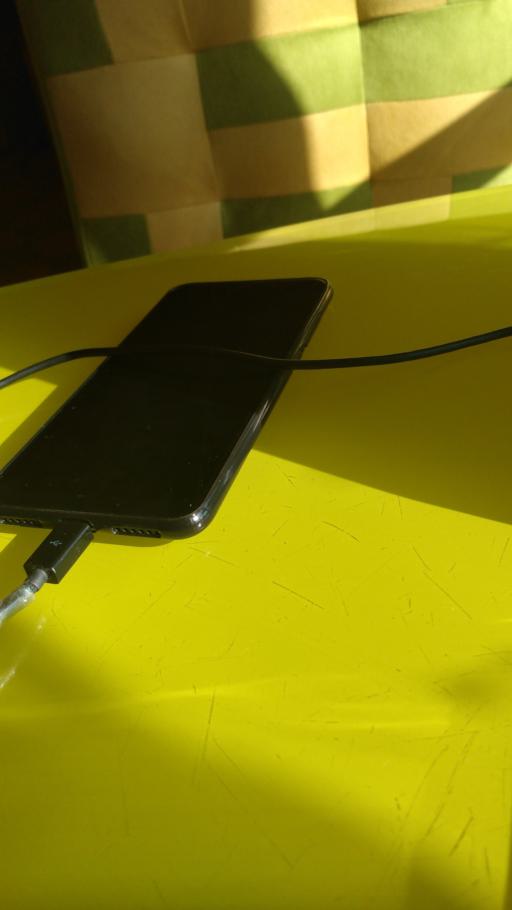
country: RU
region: Moscow
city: Rostokino
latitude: 55.8257
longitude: 37.6680
